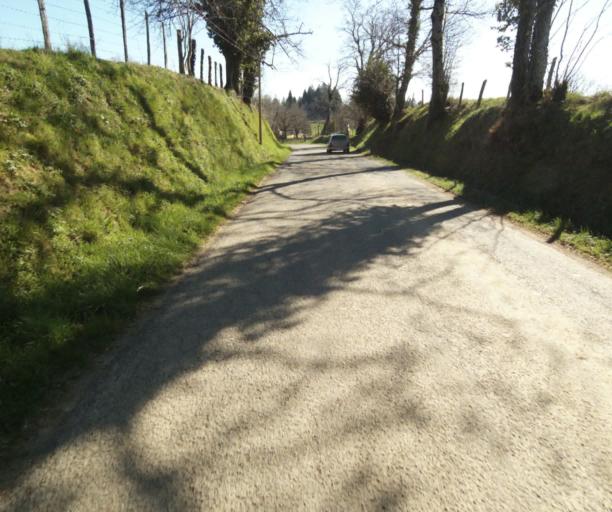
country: FR
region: Limousin
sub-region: Departement de la Correze
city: Seilhac
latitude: 45.3720
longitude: 1.7361
